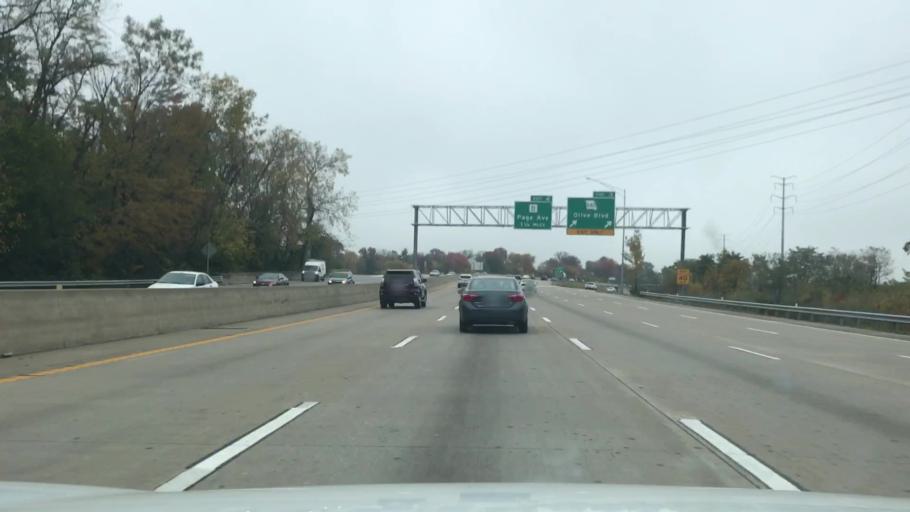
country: US
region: Missouri
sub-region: Saint Louis County
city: Olivette
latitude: 38.6707
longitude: -90.3618
